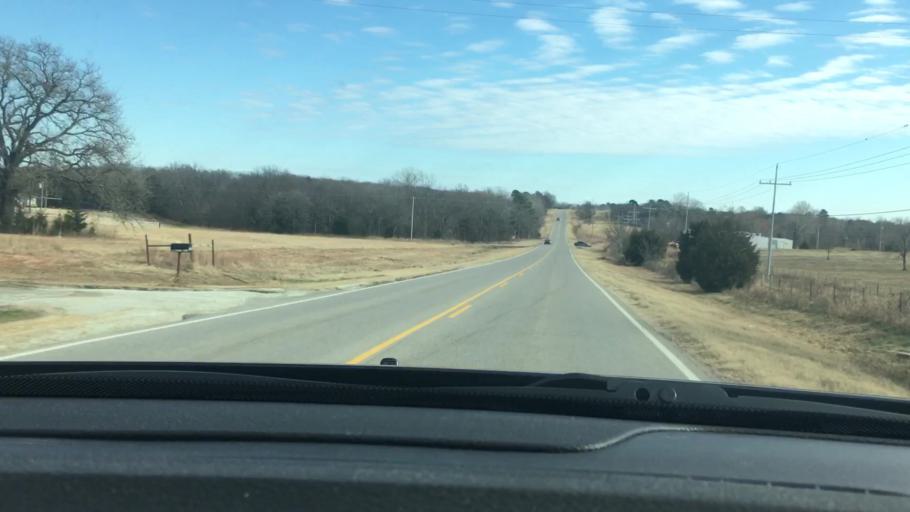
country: US
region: Oklahoma
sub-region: Pontotoc County
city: Ada
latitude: 34.7868
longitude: -96.7946
